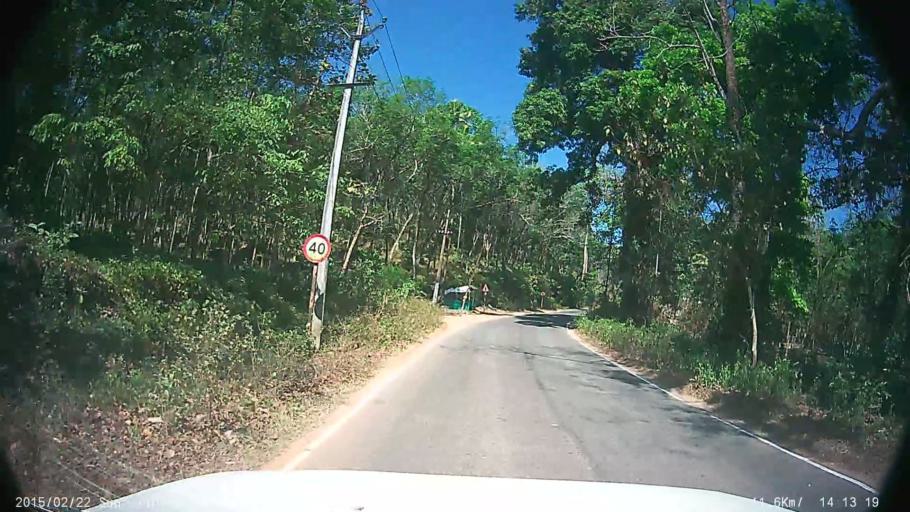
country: IN
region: Kerala
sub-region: Kottayam
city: Kottayam
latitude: 9.5382
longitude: 76.6799
